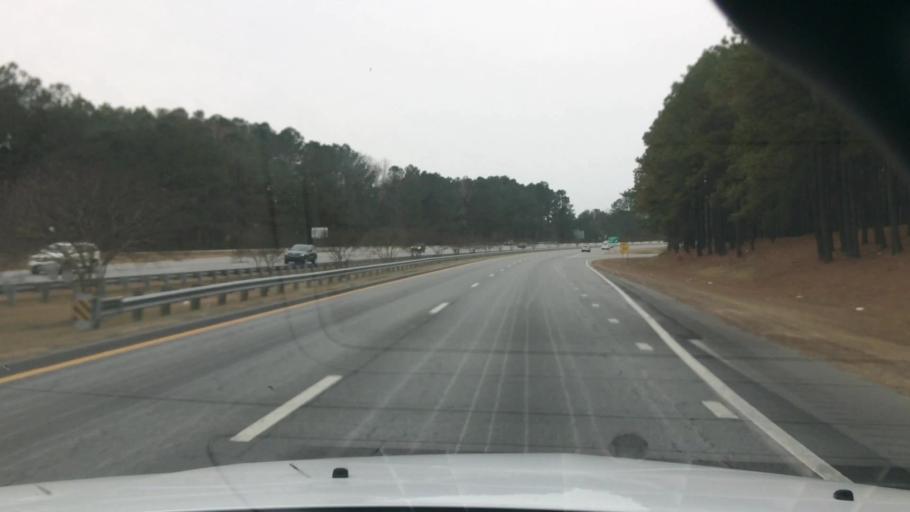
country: US
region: North Carolina
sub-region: Nash County
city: Rocky Mount
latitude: 35.9708
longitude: -77.8356
